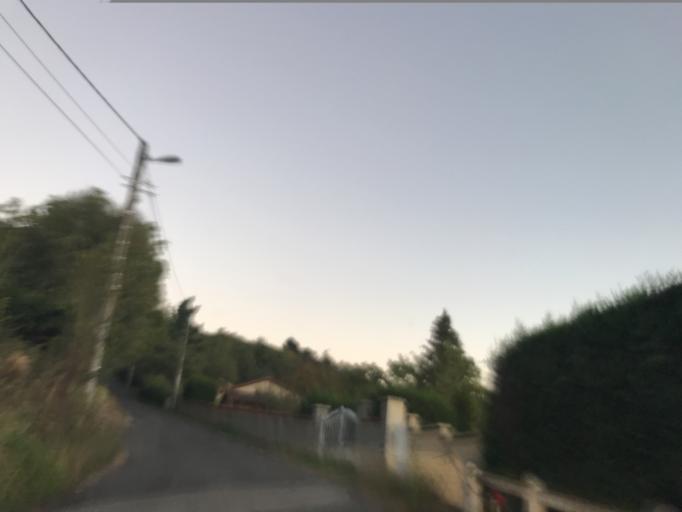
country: FR
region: Auvergne
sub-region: Departement du Puy-de-Dome
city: Thiers
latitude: 45.8451
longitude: 3.5456
